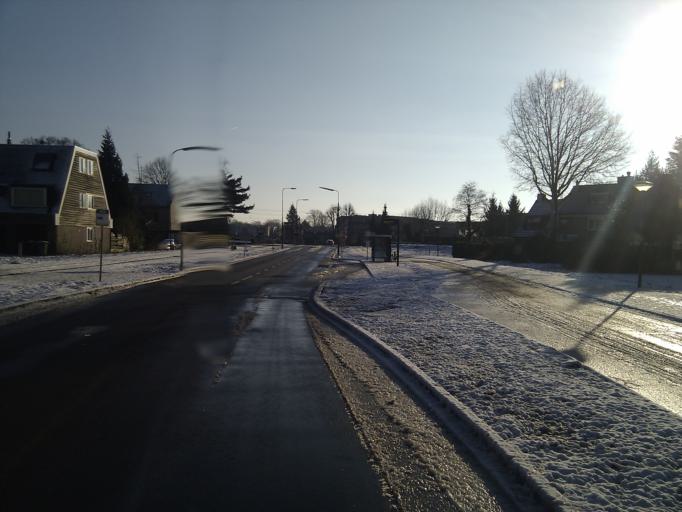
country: NL
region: Utrecht
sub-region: Gemeente De Bilt
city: De Bilt
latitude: 52.1282
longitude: 5.1922
